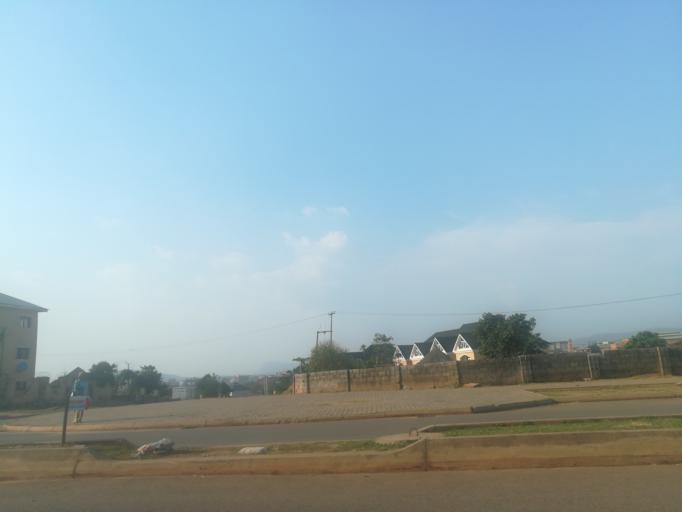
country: NG
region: Abuja Federal Capital Territory
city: Abuja
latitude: 9.0456
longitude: 7.4417
